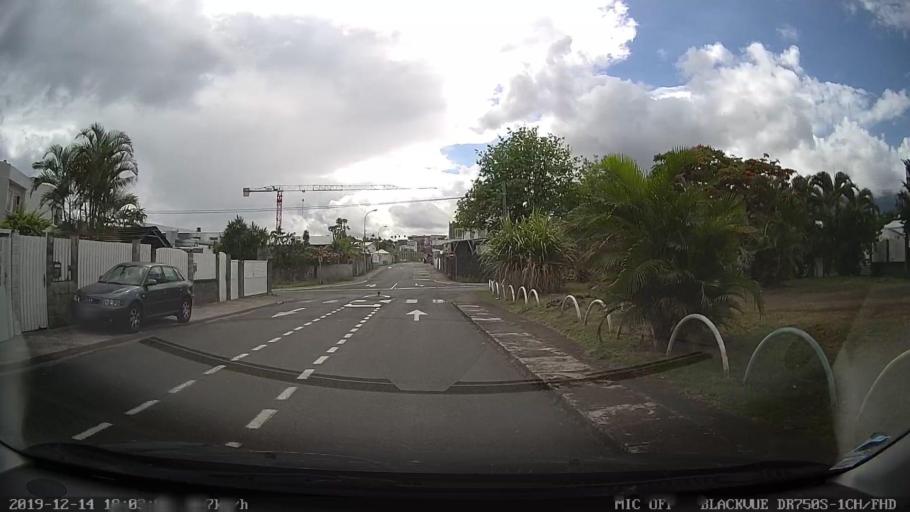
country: RE
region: Reunion
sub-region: Reunion
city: Saint-Denis
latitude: -20.9019
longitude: 55.4941
